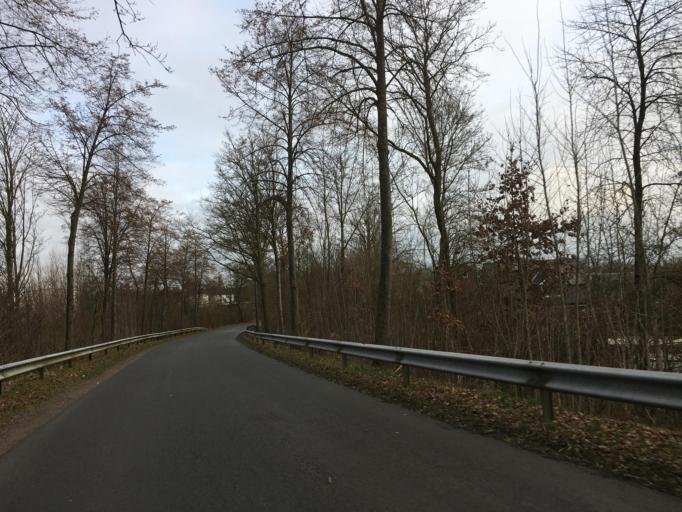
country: DE
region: North Rhine-Westphalia
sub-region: Regierungsbezirk Munster
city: Senden
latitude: 51.9056
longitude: 7.4753
